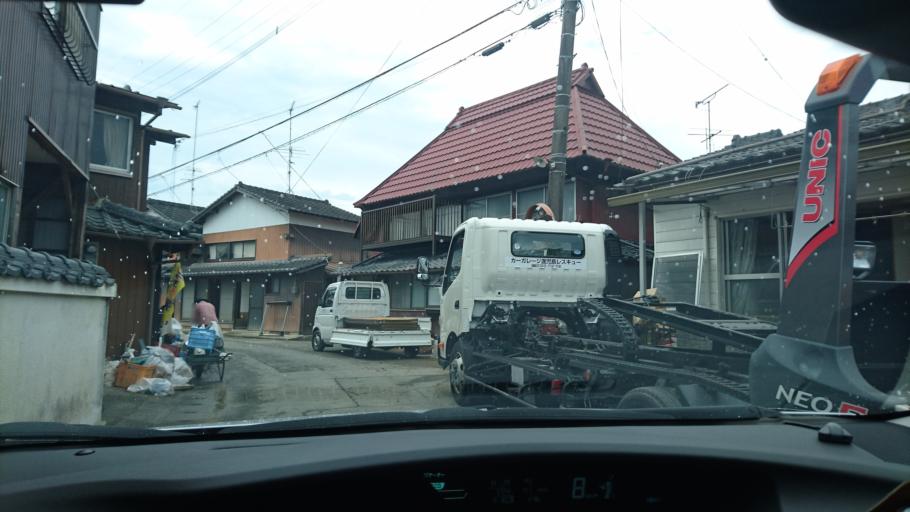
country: JP
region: Saga Prefecture
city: Takeocho-takeo
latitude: 33.2191
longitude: 130.0777
